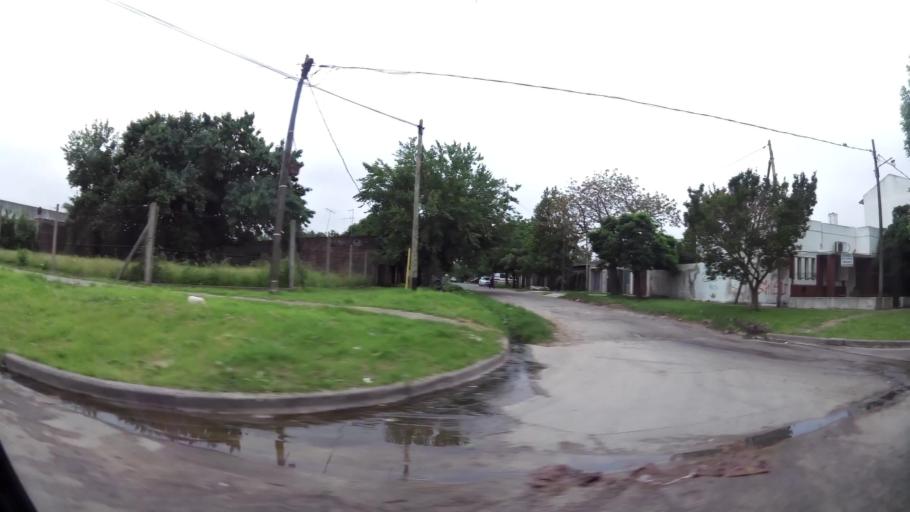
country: AR
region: Buenos Aires
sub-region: Partido de La Plata
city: La Plata
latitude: -34.9406
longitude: -57.9984
